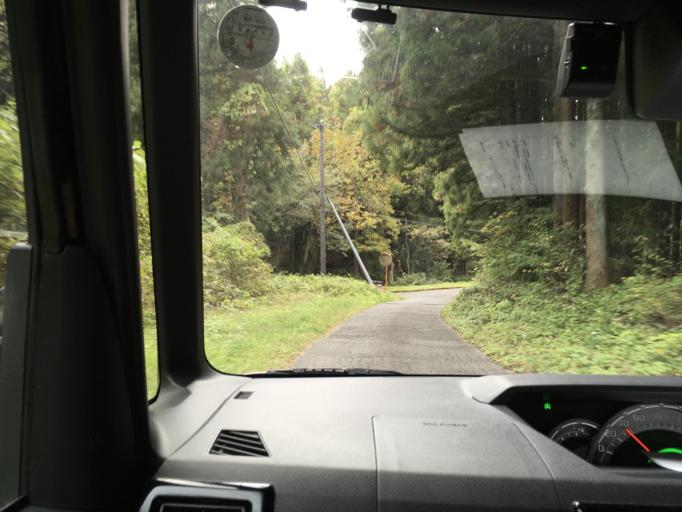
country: JP
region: Iwate
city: Mizusawa
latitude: 39.0265
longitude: 141.3563
